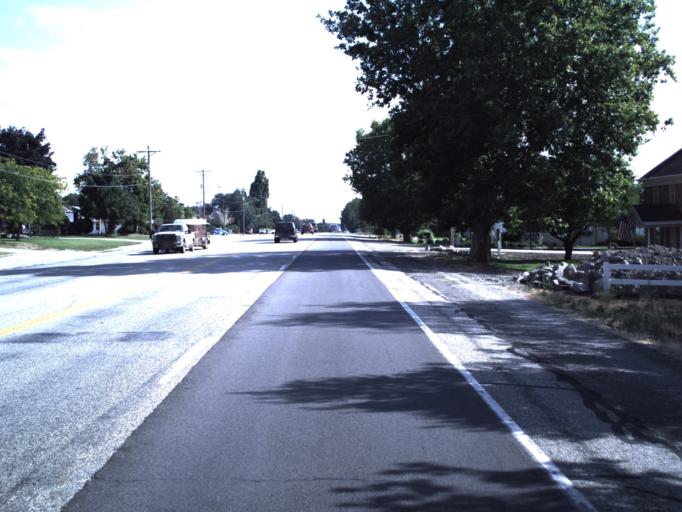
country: US
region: Utah
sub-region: Box Elder County
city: Willard
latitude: 41.4124
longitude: -112.0364
